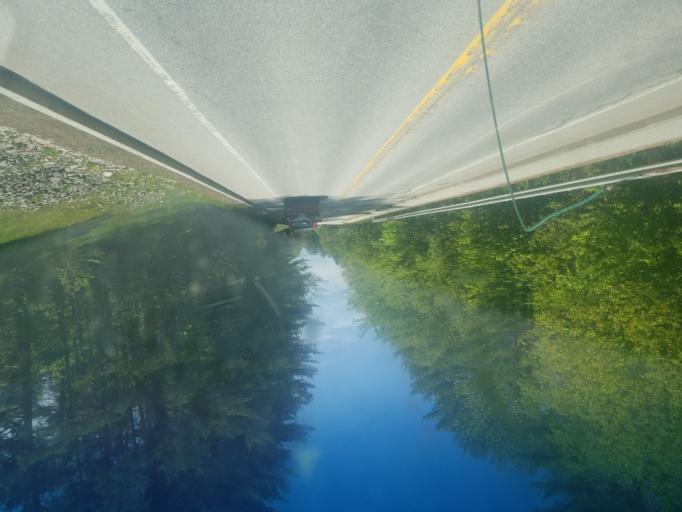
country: US
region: New Hampshire
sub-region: Grafton County
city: Plymouth
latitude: 43.7647
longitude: -71.7126
